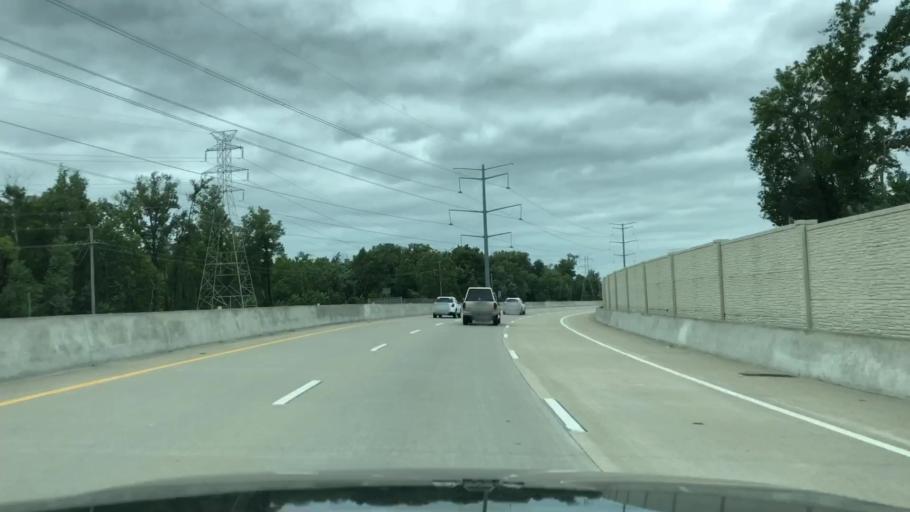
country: US
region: Missouri
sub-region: Saint Louis County
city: Town and Country
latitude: 38.6711
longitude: -90.4946
